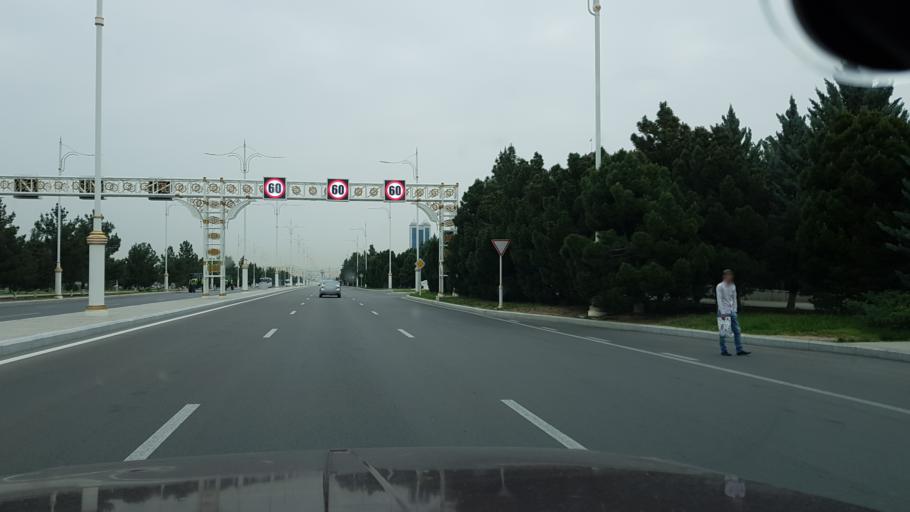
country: TM
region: Ahal
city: Ashgabat
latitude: 37.8851
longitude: 58.3876
